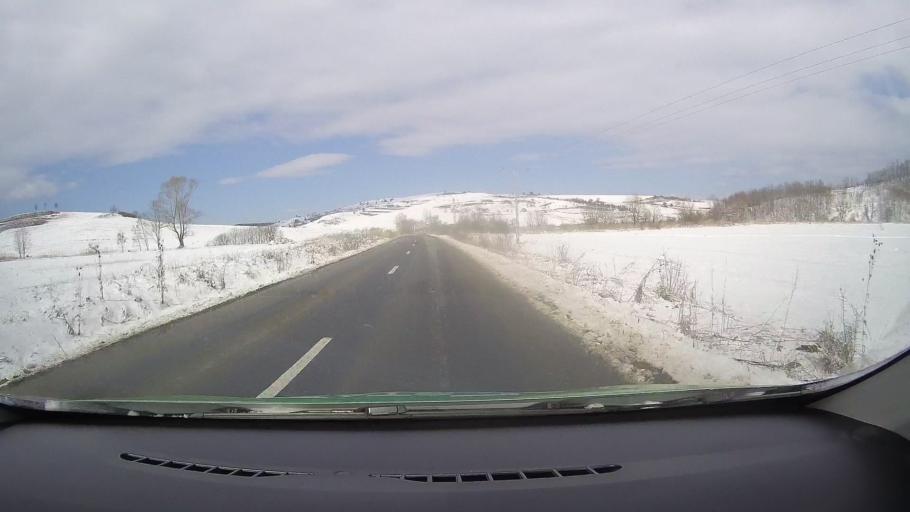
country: RO
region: Sibiu
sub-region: Comuna Altina
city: Altina
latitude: 45.9733
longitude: 24.4661
